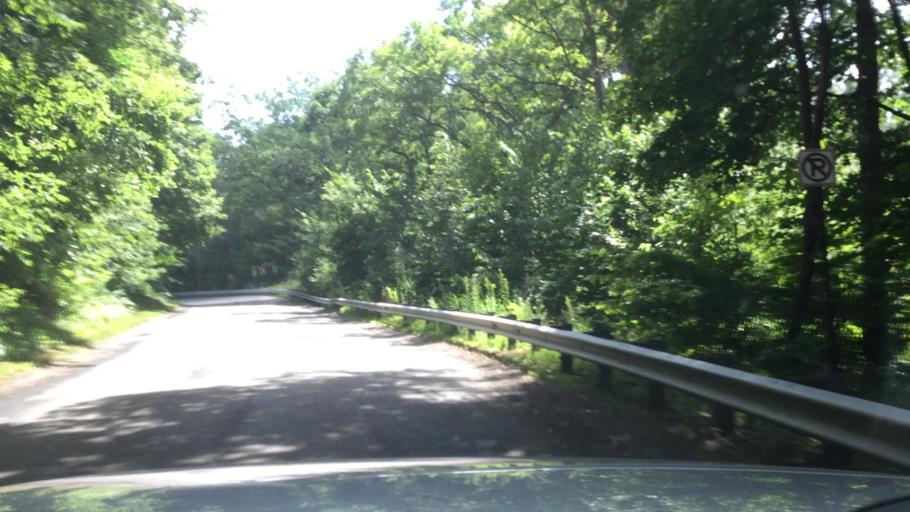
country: US
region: Michigan
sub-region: Ionia County
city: Belding
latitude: 43.1010
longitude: -85.2381
